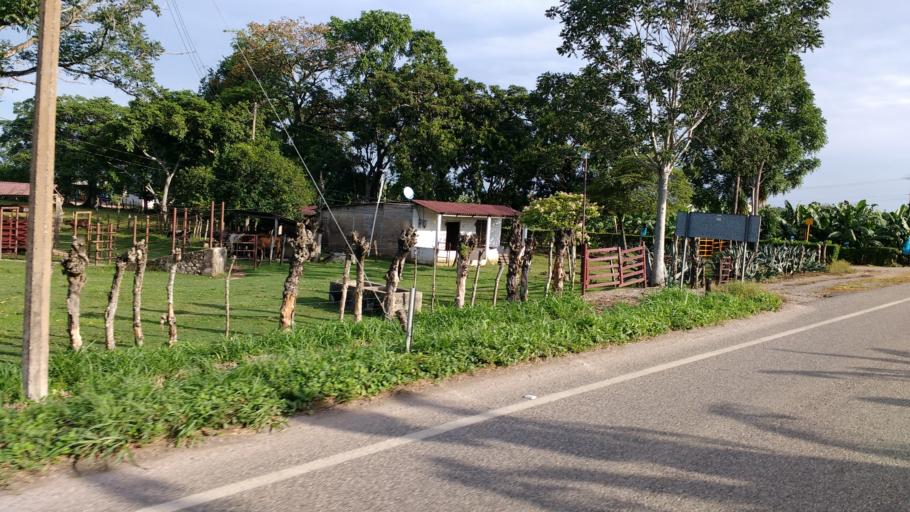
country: MX
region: Tabasco
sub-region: Teapa
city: Eureka y Belen
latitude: 17.6186
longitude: -92.9634
